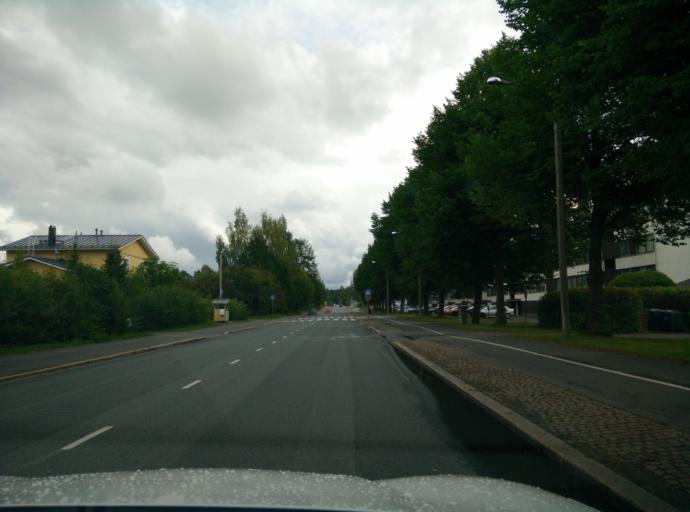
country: FI
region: Haeme
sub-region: Haemeenlinna
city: Haemeenlinna
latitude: 60.9982
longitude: 24.4284
